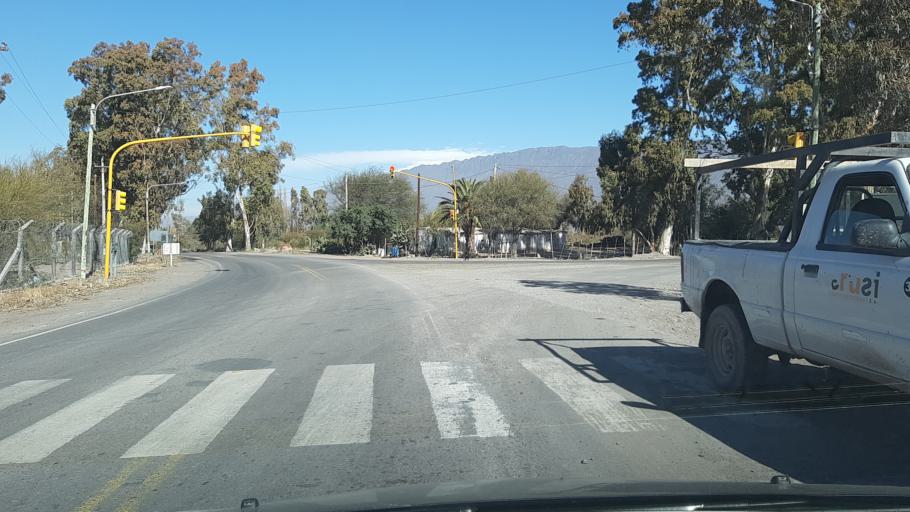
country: AR
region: San Juan
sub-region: Departamento de Zonda
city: Zonda
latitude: -31.5465
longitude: -68.7193
